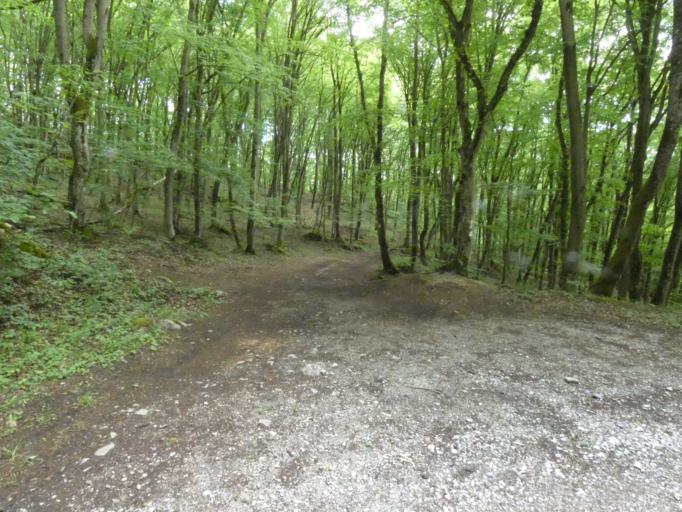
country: HU
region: Borsod-Abauj-Zemplen
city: Rudabanya
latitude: 48.5410
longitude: 20.6580
